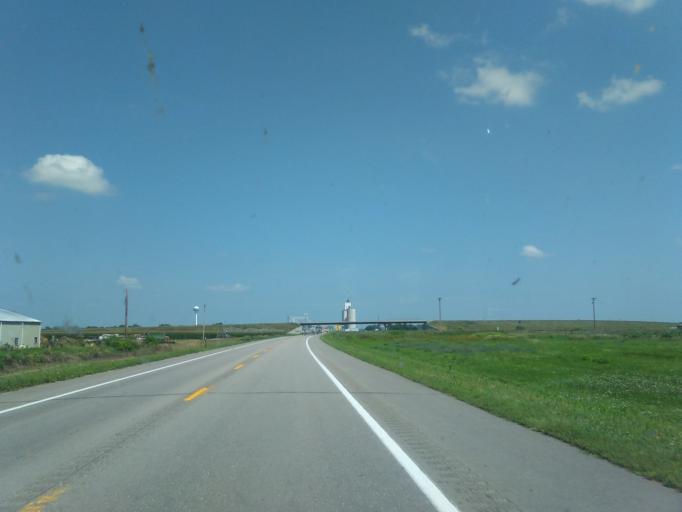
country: US
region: Nebraska
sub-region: Phelps County
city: Holdrege
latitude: 40.7199
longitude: -99.3917
